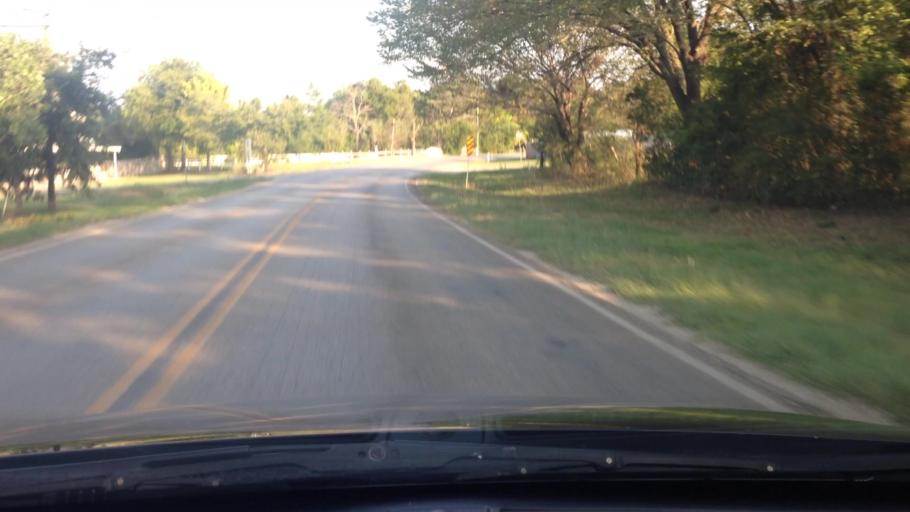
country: US
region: Texas
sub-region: Tarrant County
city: Rendon
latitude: 32.5842
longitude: -97.2427
